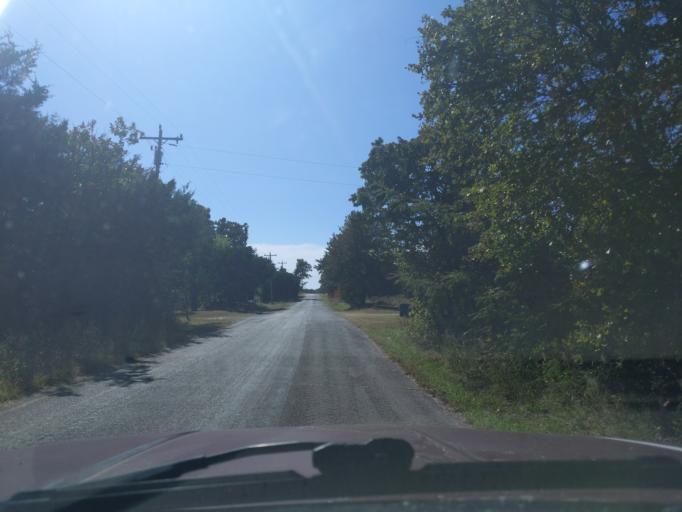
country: US
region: Oklahoma
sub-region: Creek County
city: Bristow
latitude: 35.6996
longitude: -96.4099
